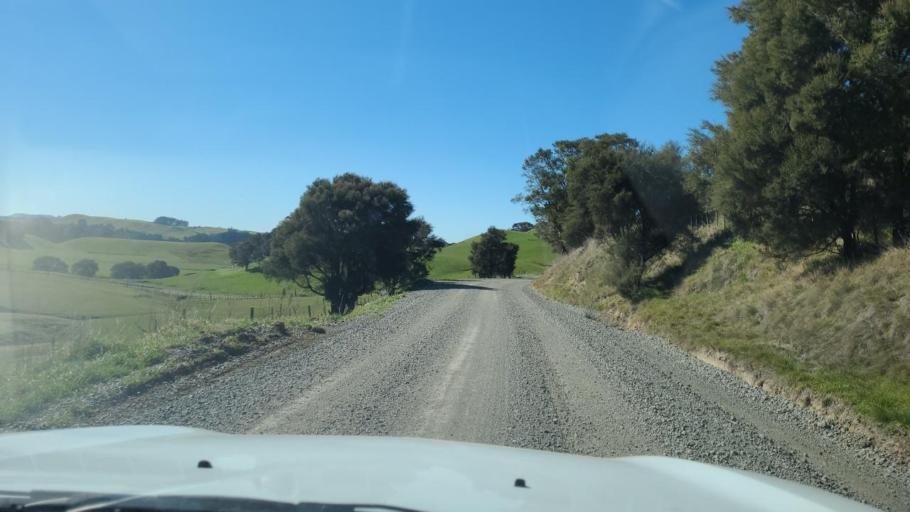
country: NZ
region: Hawke's Bay
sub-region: Napier City
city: Taradale
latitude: -39.4463
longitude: 176.5545
